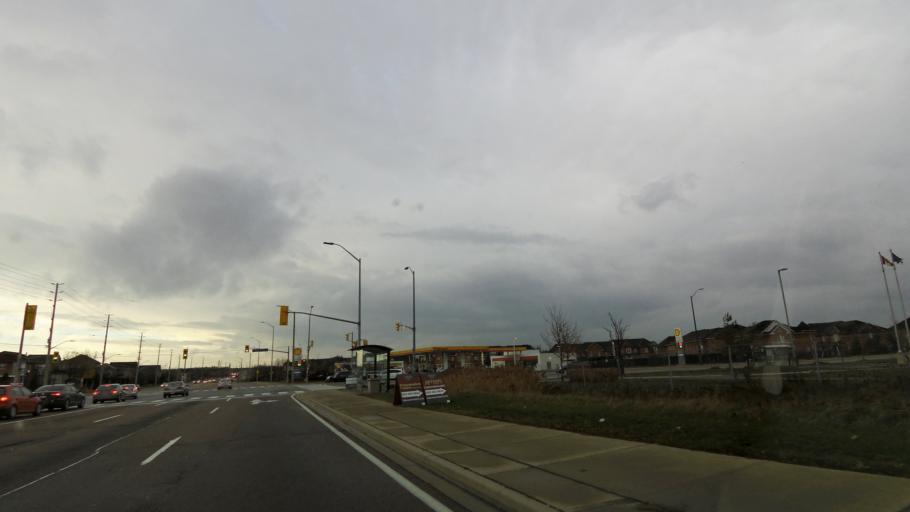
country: CA
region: Ontario
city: Mississauga
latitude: 43.6235
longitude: -79.7113
